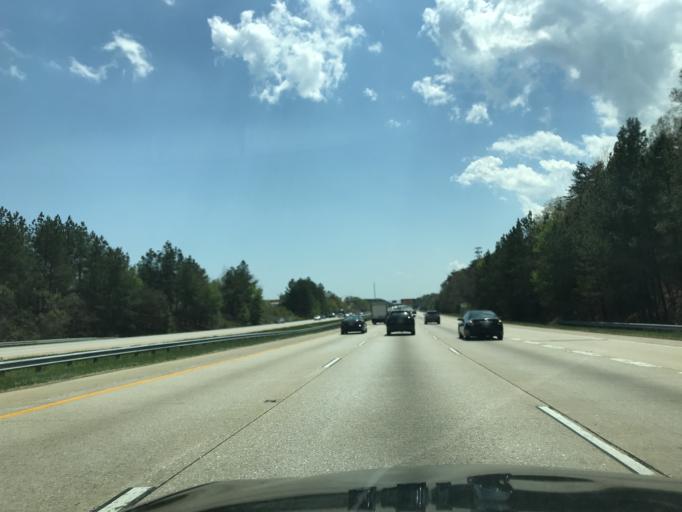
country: US
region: Maryland
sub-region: Anne Arundel County
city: South Gate
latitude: 39.1050
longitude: -76.6300
